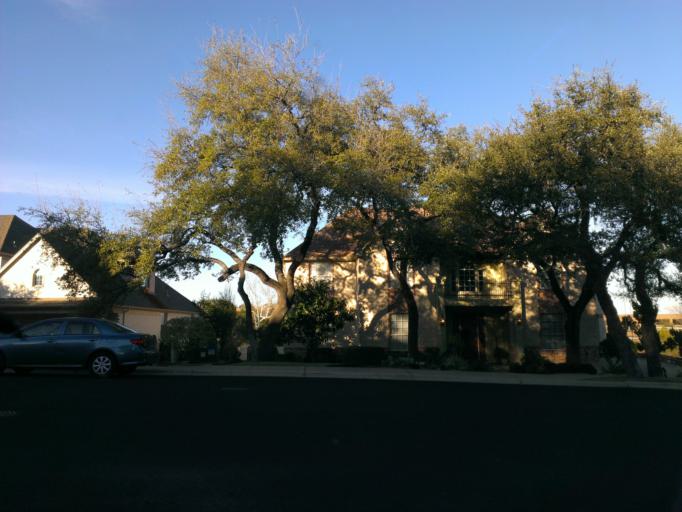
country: US
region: Texas
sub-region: Travis County
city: Rollingwood
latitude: 30.2743
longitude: -97.8193
